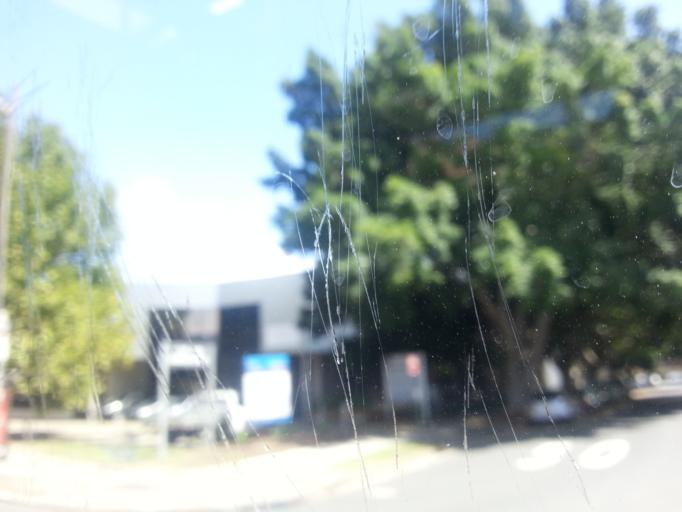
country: AU
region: New South Wales
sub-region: City of Sydney
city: Alexandria
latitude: -33.9022
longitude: 151.1982
